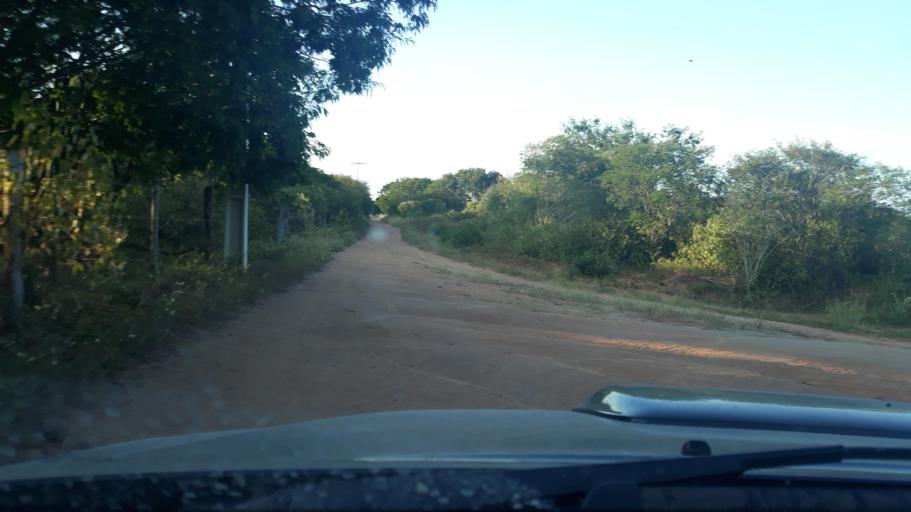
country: BR
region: Bahia
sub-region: Riacho De Santana
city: Riacho de Santana
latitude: -13.8515
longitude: -43.0533
